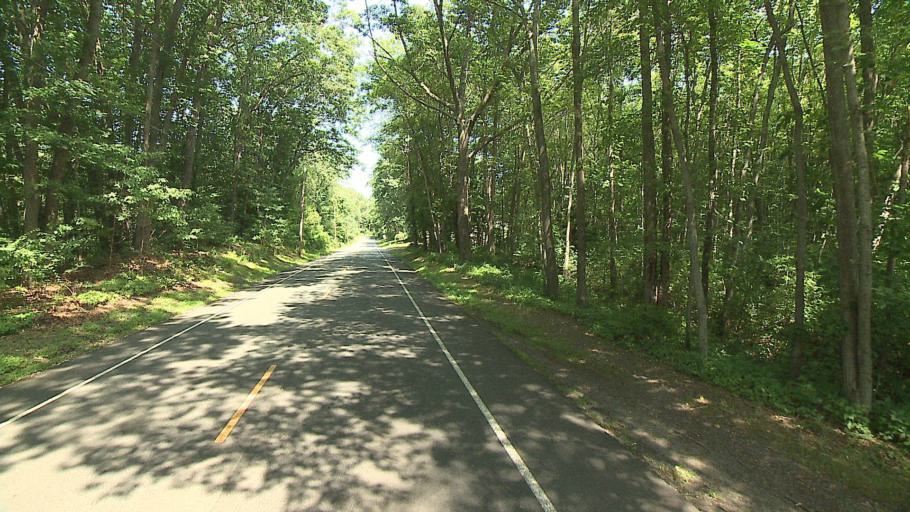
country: US
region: Connecticut
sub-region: Fairfield County
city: Trumbull
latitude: 41.2803
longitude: -73.2947
